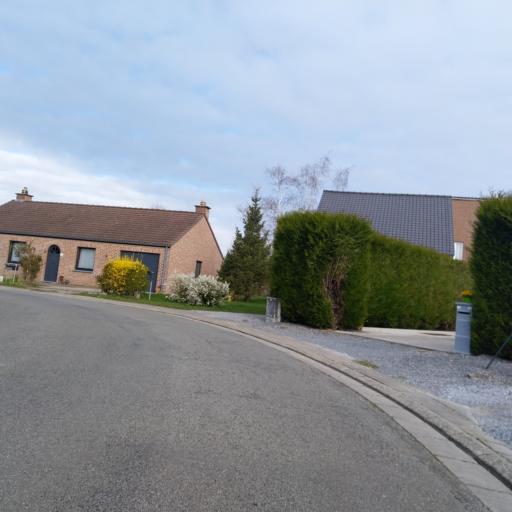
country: BE
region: Wallonia
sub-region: Province du Hainaut
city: Lens
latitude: 50.5613
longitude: 3.8996
